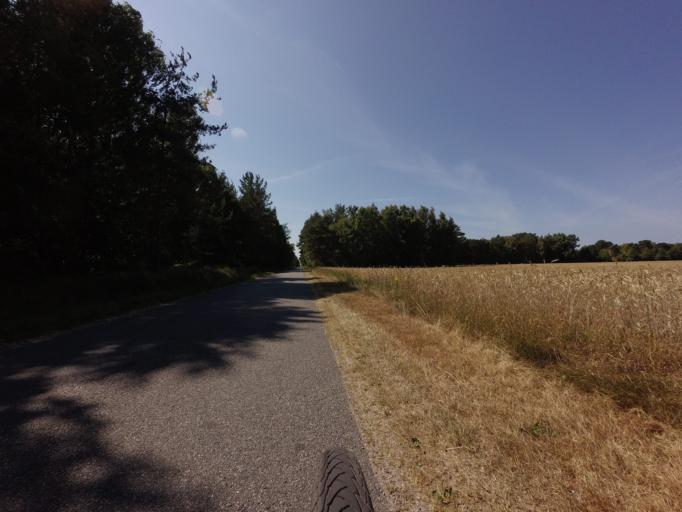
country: DK
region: North Denmark
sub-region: Laeso Kommune
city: Byrum
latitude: 57.2926
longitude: 10.9500
